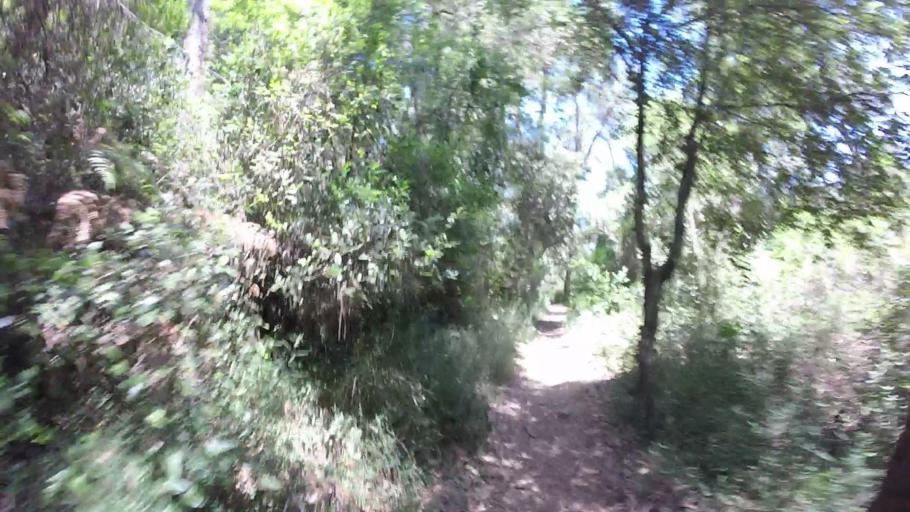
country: FR
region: Provence-Alpes-Cote d'Azur
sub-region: Departement des Alpes-Maritimes
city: Le Cannet
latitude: 43.5973
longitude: 7.0263
